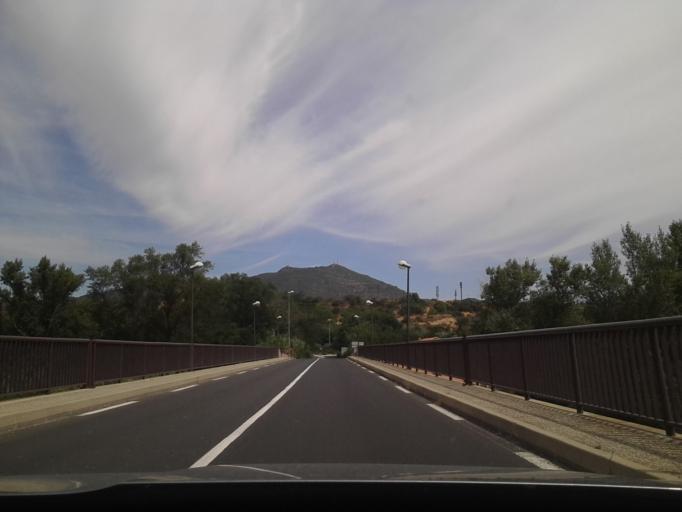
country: FR
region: Languedoc-Roussillon
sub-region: Departement des Pyrenees-Orientales
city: Millas
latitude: 42.6967
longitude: 2.6970
